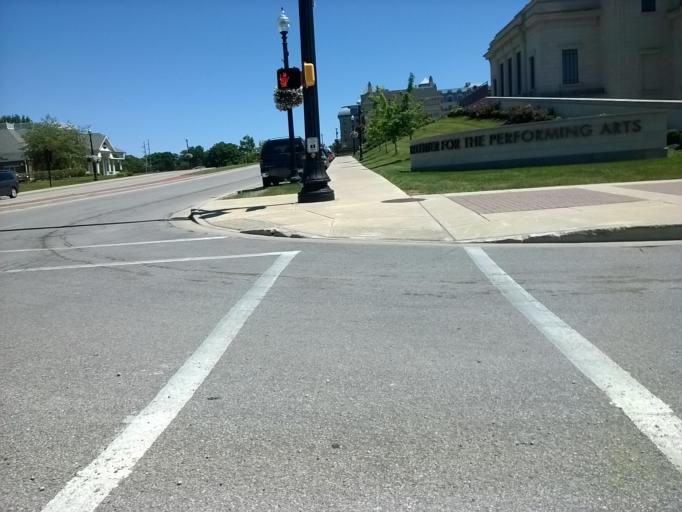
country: US
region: Indiana
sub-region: Hamilton County
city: Carmel
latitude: 39.9704
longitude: -86.1312
